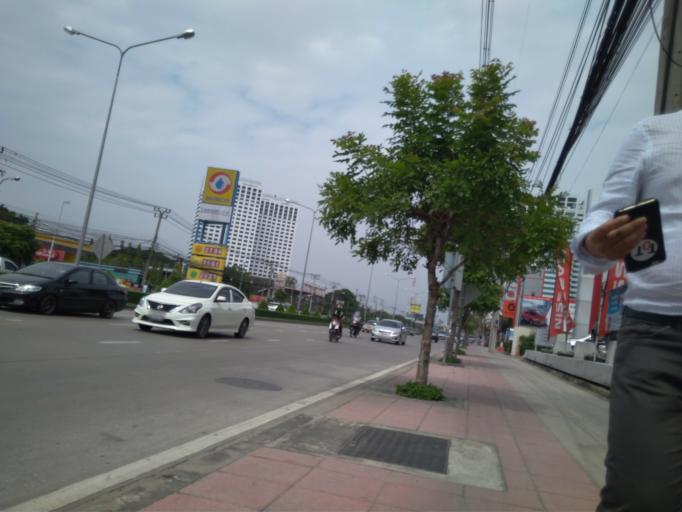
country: TH
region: Bangkok
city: Suan Luang
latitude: 13.7269
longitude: 100.6418
